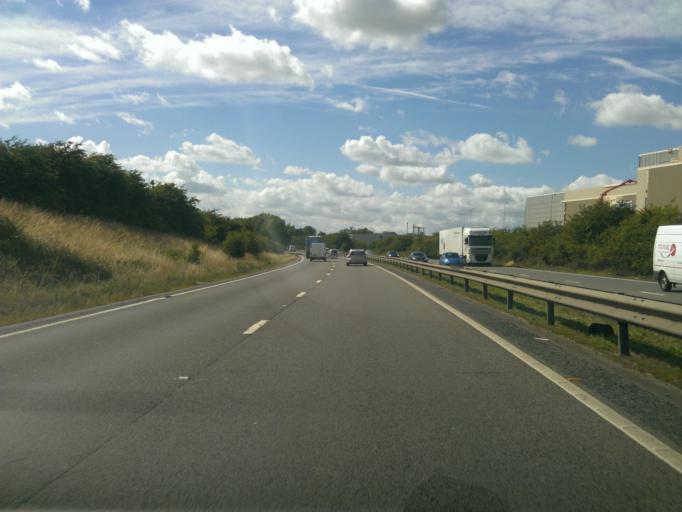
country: GB
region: England
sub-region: Northamptonshire
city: Thrapston
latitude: 52.3916
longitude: -0.5681
